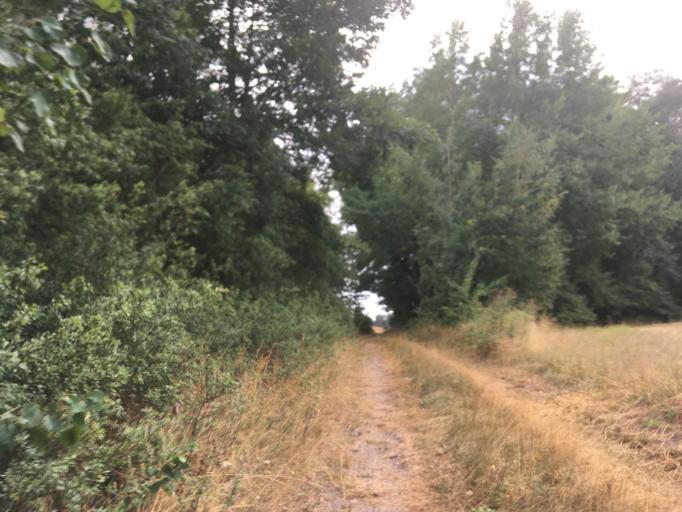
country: DE
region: Brandenburg
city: Chorin
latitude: 52.9384
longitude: 13.8779
